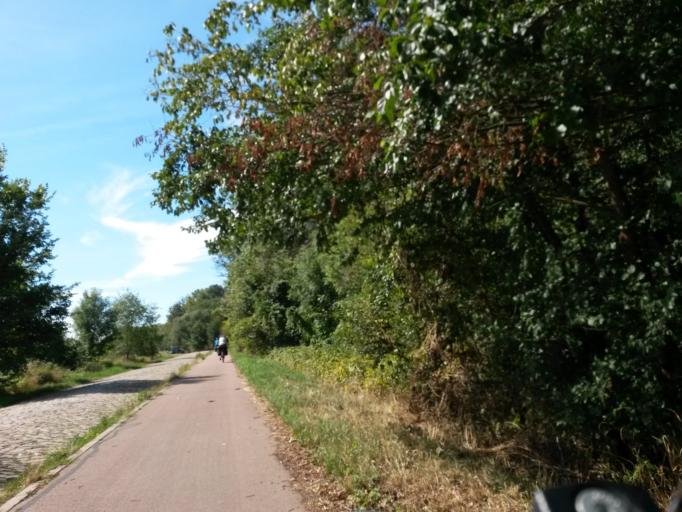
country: DE
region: Saxony-Anhalt
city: Coswig
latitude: 51.8728
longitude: 12.4480
